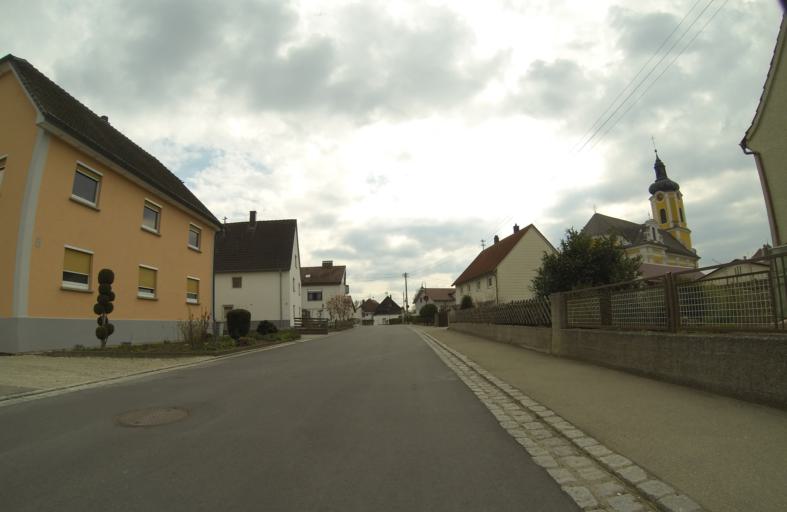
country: DE
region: Baden-Wuerttemberg
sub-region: Tuebingen Region
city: Erbach
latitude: 48.3024
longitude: 9.9017
